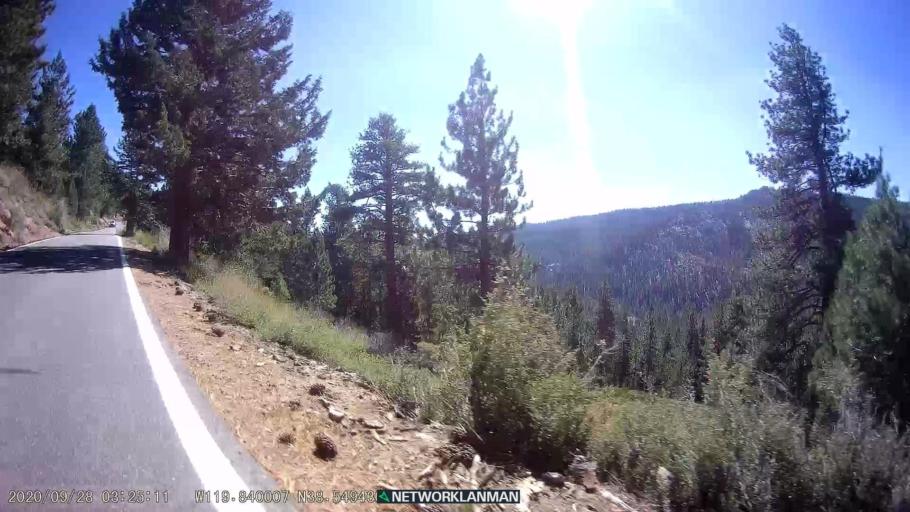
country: US
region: Nevada
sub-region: Douglas County
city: Gardnerville Ranchos
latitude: 38.5494
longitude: -119.8398
